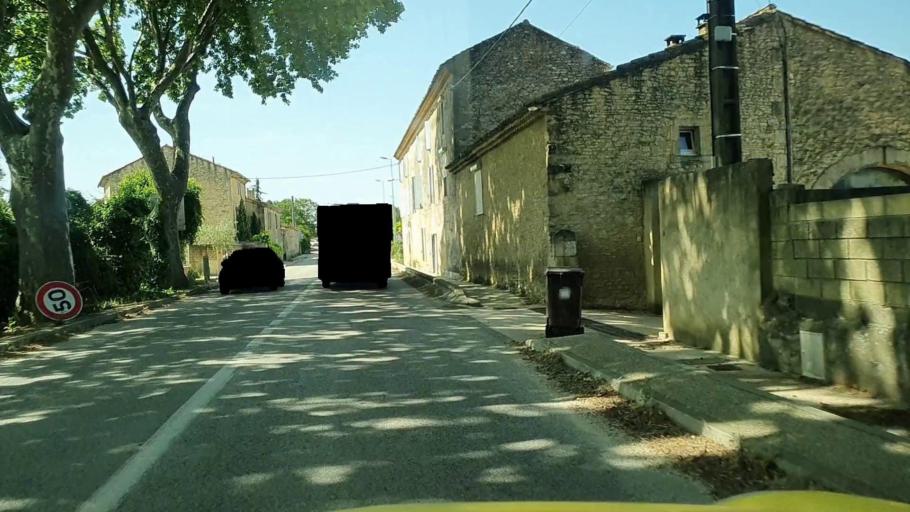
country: FR
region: Languedoc-Roussillon
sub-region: Departement du Gard
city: Remoulins
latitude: 43.9560
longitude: 4.5678
